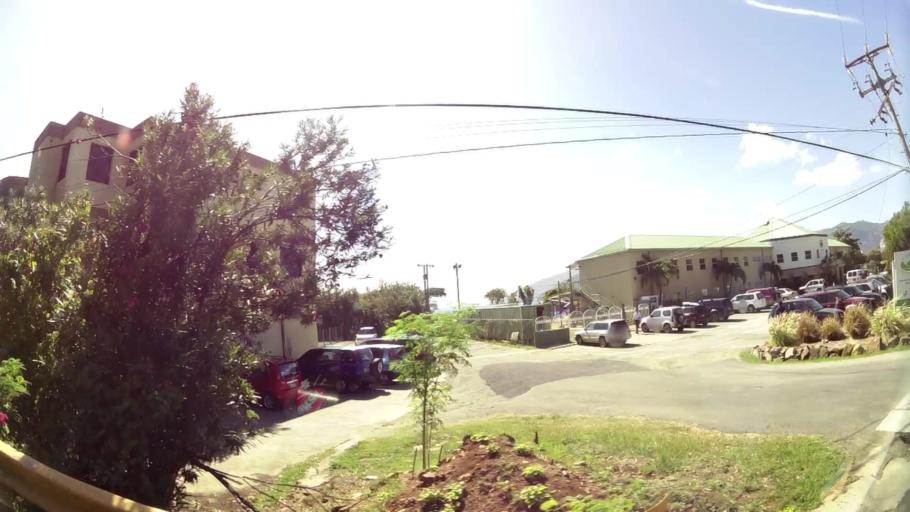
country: VG
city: Tortola
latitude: 18.4153
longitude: -64.5947
